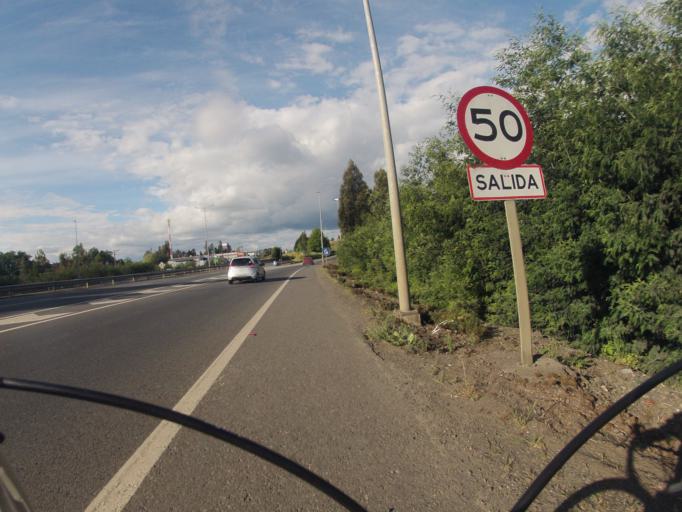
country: CL
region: Araucania
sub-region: Provincia de Cautin
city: Temuco
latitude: -38.7881
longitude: -72.6156
